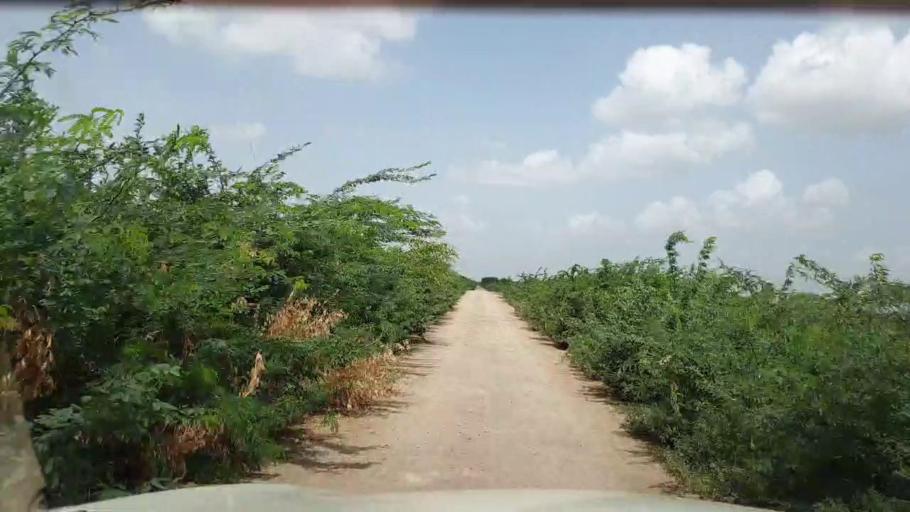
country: PK
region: Sindh
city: Kadhan
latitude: 24.4219
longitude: 68.8290
